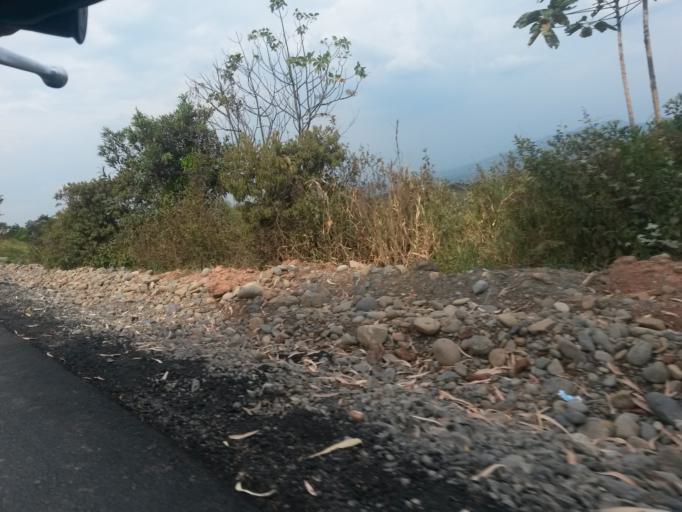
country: CO
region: Cauca
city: Buenos Aires
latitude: 3.0491
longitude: -76.6378
